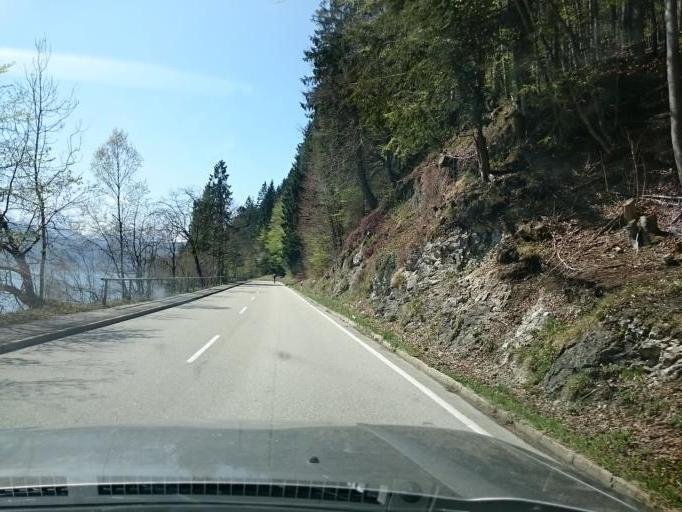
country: DE
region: Bavaria
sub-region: Upper Bavaria
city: Schlehdorf
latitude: 47.6137
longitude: 11.3388
